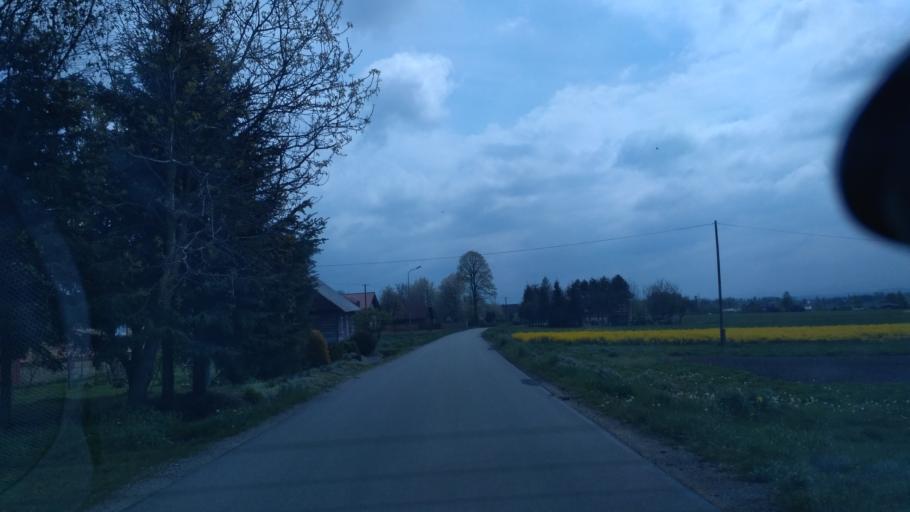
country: PL
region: Subcarpathian Voivodeship
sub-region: Powiat brzozowski
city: Jablonica Polska
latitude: 49.6808
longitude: 21.8995
